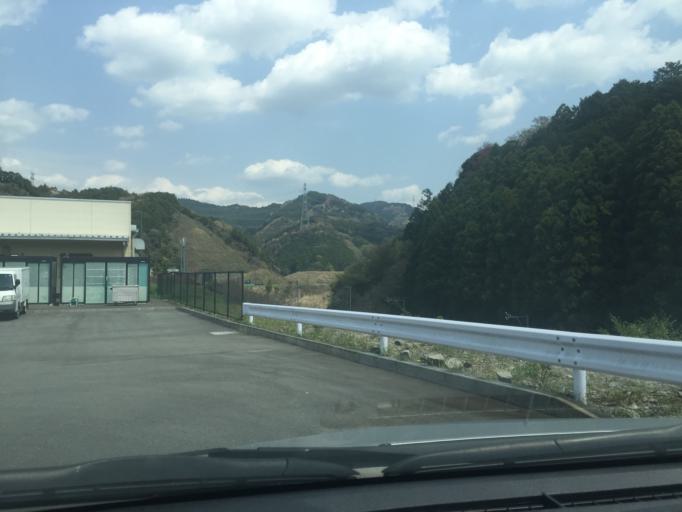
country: JP
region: Shizuoka
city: Kakegawa
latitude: 34.8382
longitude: 138.0352
